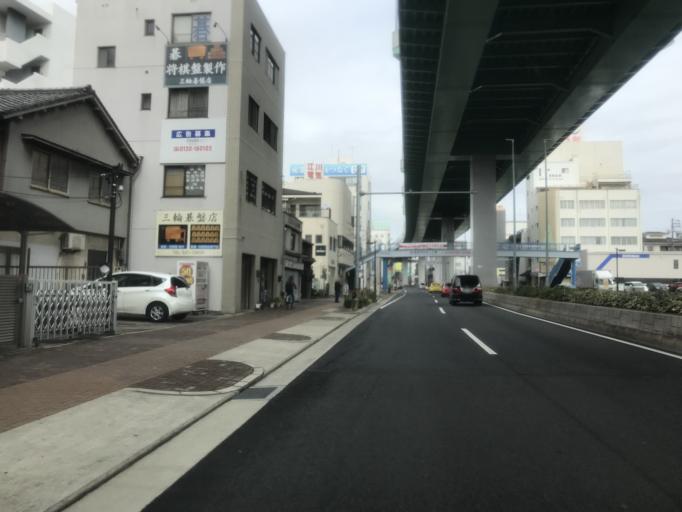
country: JP
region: Aichi
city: Nagoya-shi
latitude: 35.1874
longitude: 136.8907
